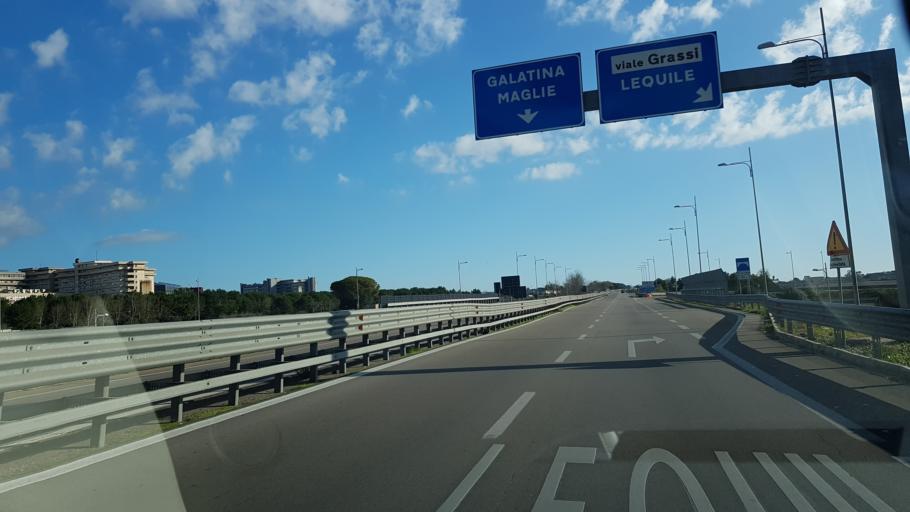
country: IT
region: Apulia
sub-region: Provincia di Lecce
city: Lequile
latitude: 40.3261
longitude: 18.1523
